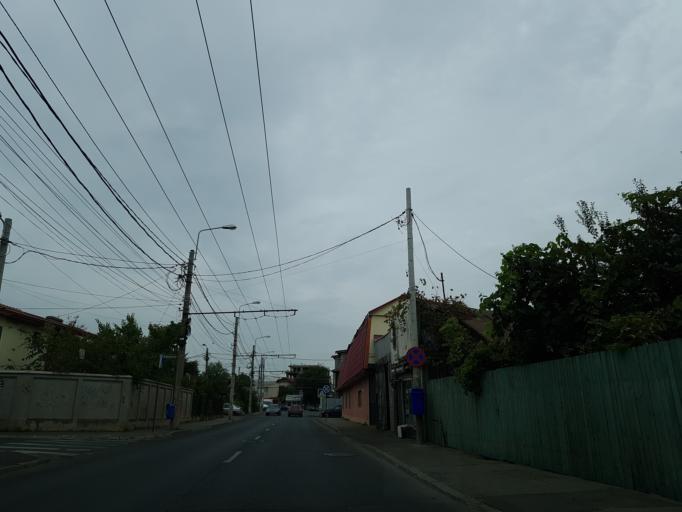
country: RO
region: Ilfov
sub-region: Comuna Fundeni-Dobroesti
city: Fundeni
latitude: 44.4702
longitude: 26.1514
